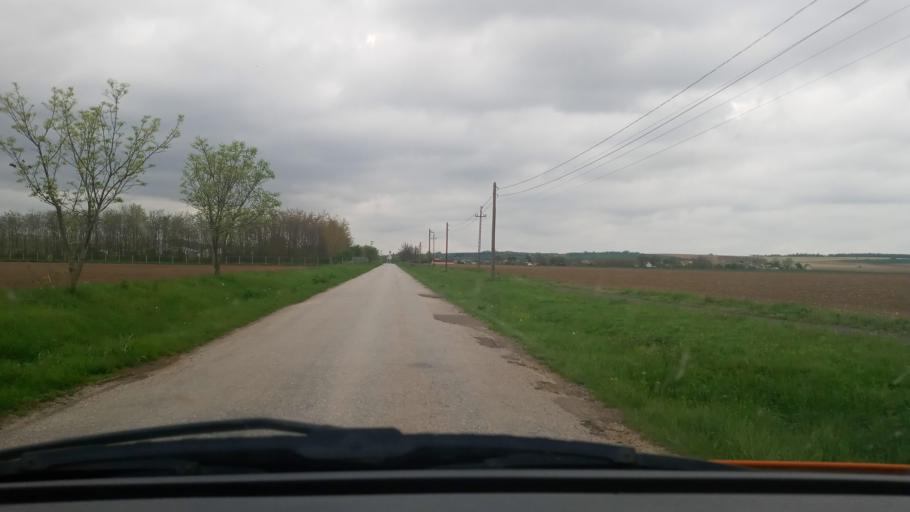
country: HU
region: Baranya
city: Boly
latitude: 45.9903
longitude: 18.5599
